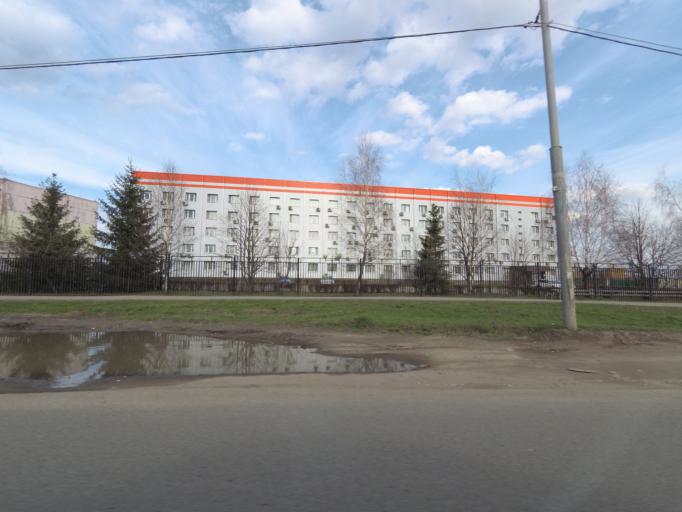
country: RU
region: Moskovskaya
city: Lobnya
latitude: 55.9846
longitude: 37.4180
